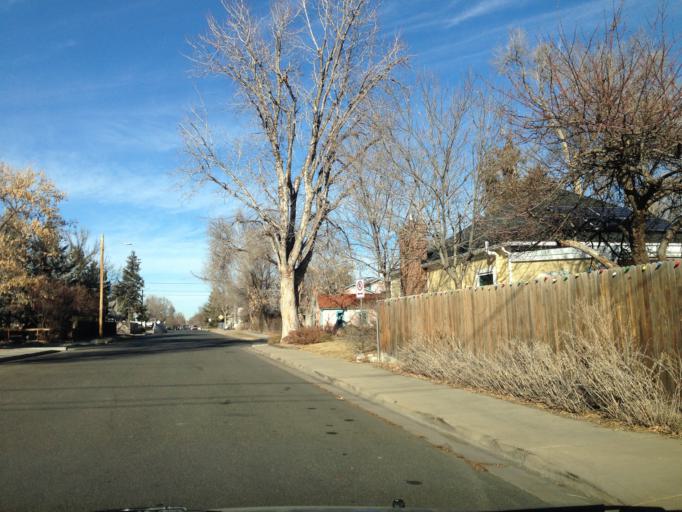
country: US
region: Colorado
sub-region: Boulder County
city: Louisville
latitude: 39.9726
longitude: -105.1321
